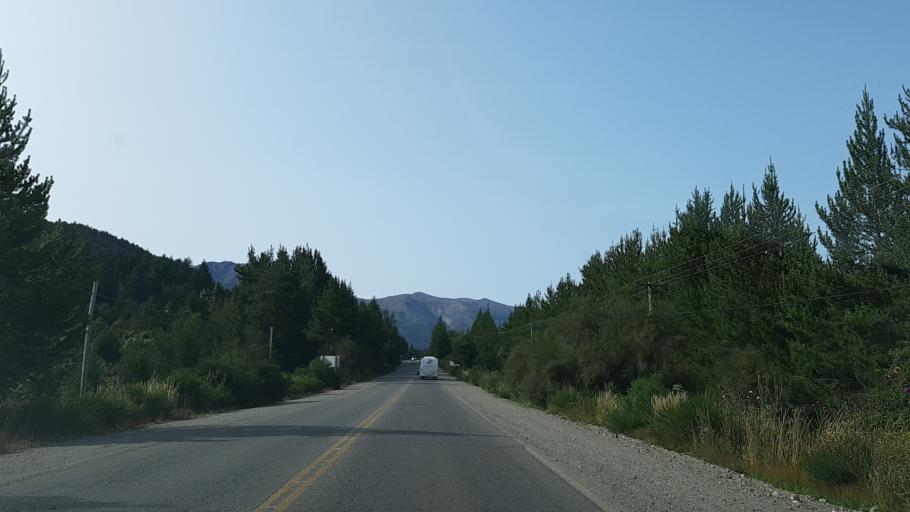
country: AR
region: Rio Negro
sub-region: Departamento de Bariloche
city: San Carlos de Bariloche
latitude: -41.1455
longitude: -71.4101
